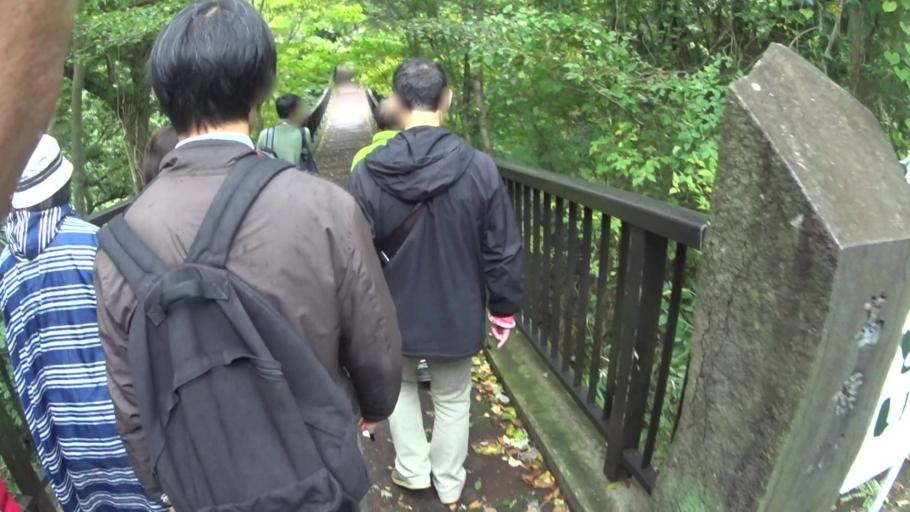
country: JP
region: Kanagawa
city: Hadano
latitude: 35.3830
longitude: 139.2193
